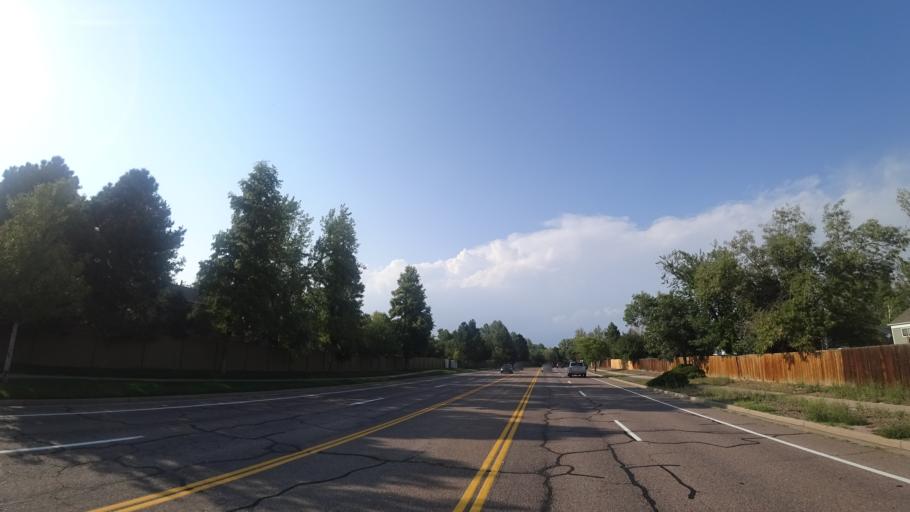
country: US
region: Colorado
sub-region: Arapahoe County
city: Dove Valley
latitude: 39.6124
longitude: -104.7446
